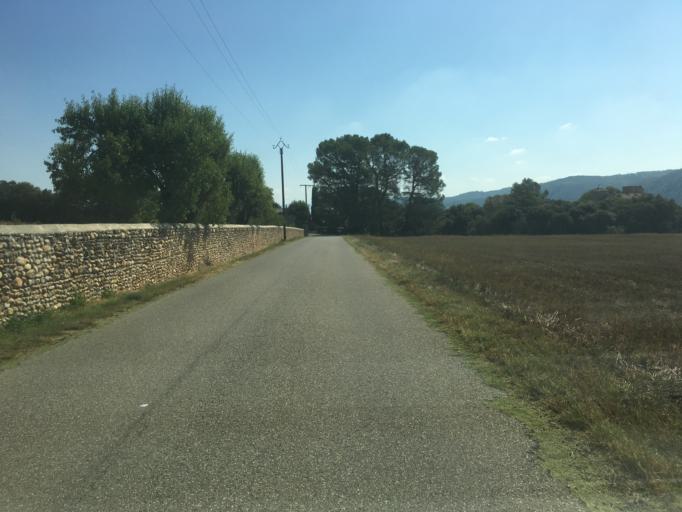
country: FR
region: Provence-Alpes-Cote d'Azur
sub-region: Departement des Alpes-de-Haute-Provence
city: Valensole
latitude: 43.8924
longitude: 5.9760
